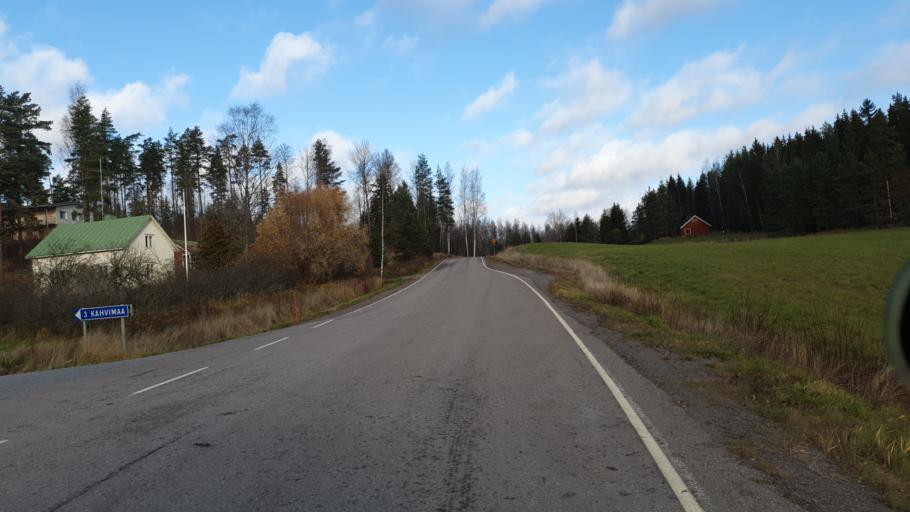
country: FI
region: Uusimaa
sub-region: Helsinki
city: Vihti
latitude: 60.2685
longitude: 24.3034
